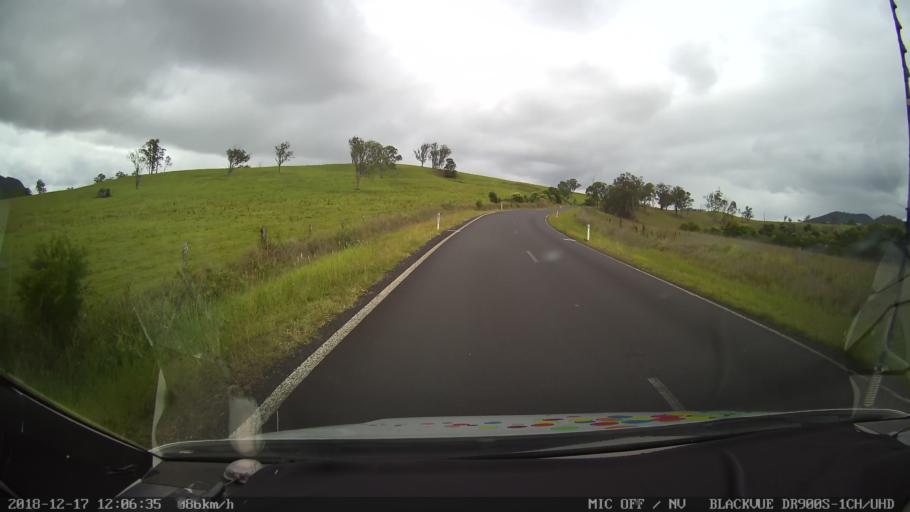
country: AU
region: New South Wales
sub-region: Kyogle
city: Kyogle
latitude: -28.4806
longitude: 152.5660
